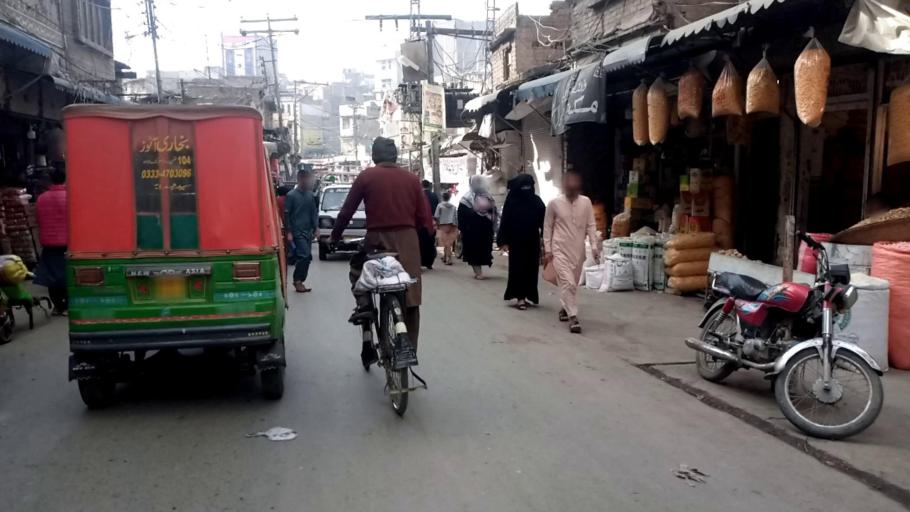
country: PK
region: Khyber Pakhtunkhwa
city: Peshawar
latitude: 34.0082
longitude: 71.5745
